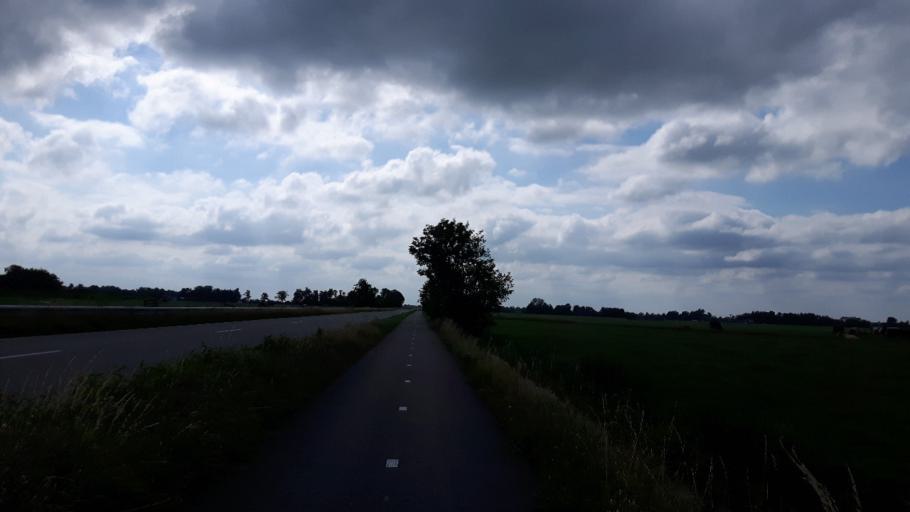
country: NL
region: Utrecht
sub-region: Gemeente Woerden
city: Woerden
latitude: 52.1339
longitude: 4.8605
